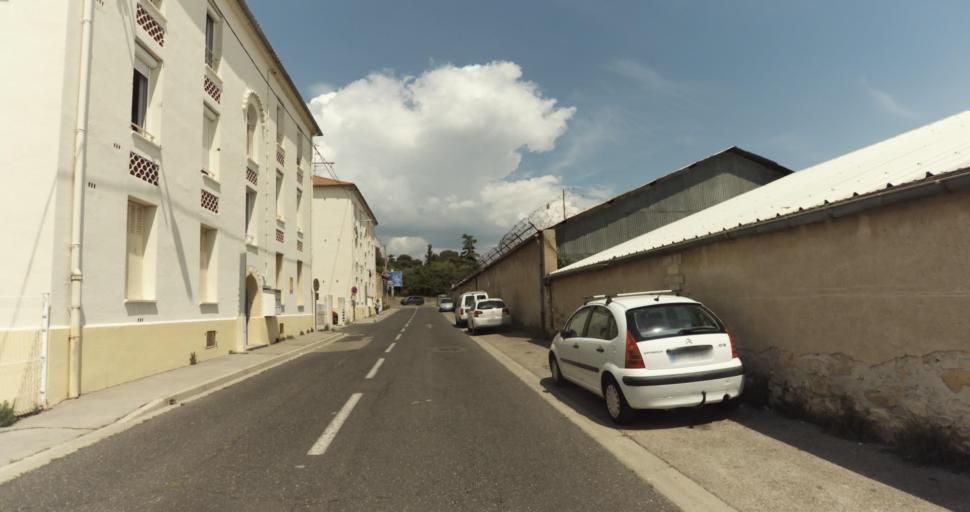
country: FR
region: Languedoc-Roussillon
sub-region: Departement du Gard
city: Nimes
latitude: 43.8494
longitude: 4.3690
